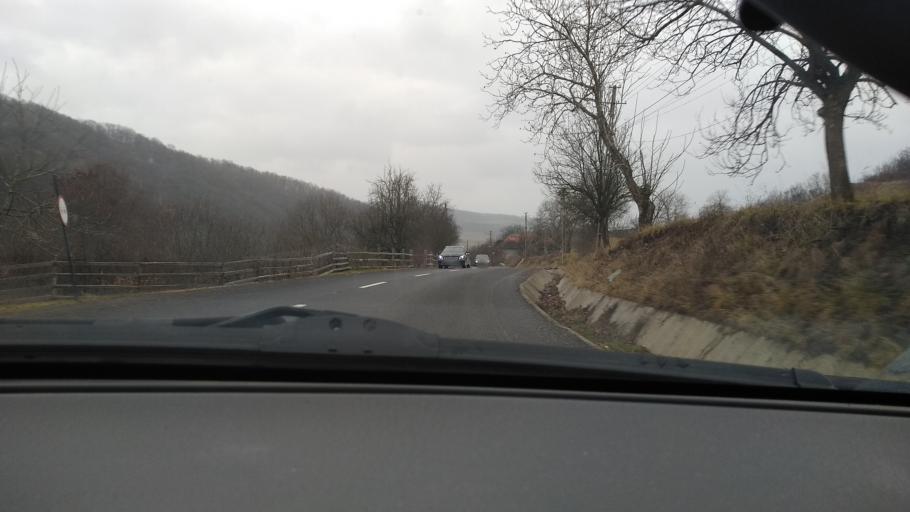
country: RO
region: Mures
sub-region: Comuna Magherani
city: Magherani
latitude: 46.5722
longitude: 24.9235
